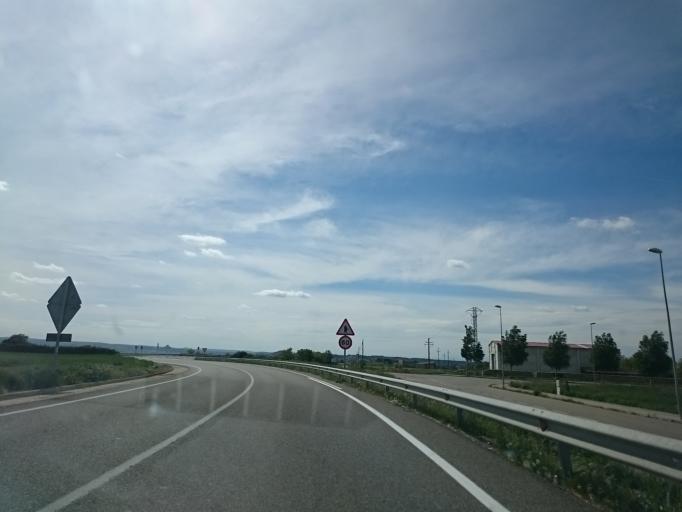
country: ES
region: Catalonia
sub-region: Provincia de Lleida
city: Sant Guim de Freixenet
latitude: 41.6435
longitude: 1.4173
